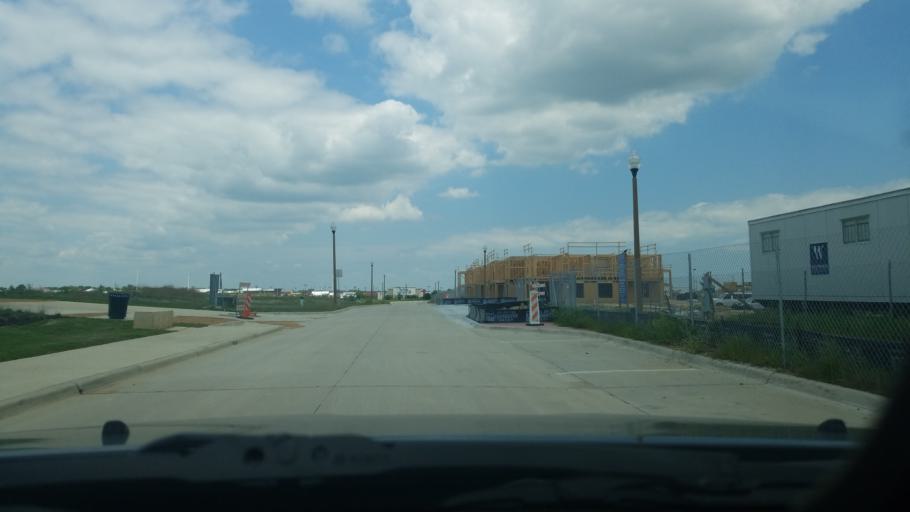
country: US
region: Texas
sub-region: Denton County
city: Denton
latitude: 33.2266
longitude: -97.1646
